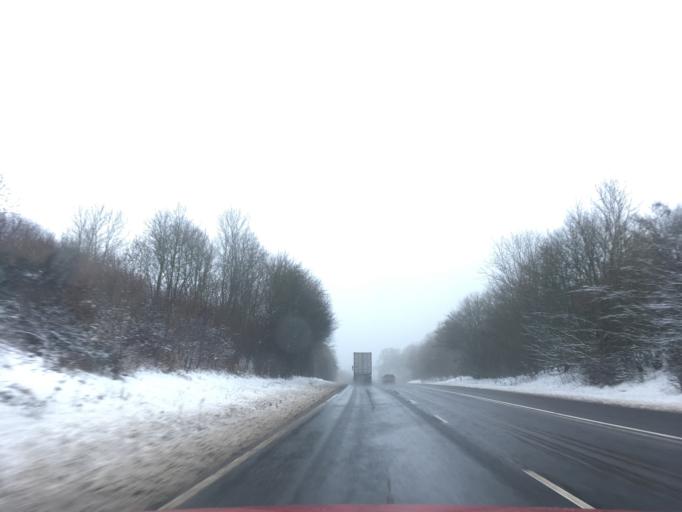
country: GB
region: England
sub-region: Warwickshire
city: Stratford-upon-Avon
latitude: 52.2176
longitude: -1.7111
